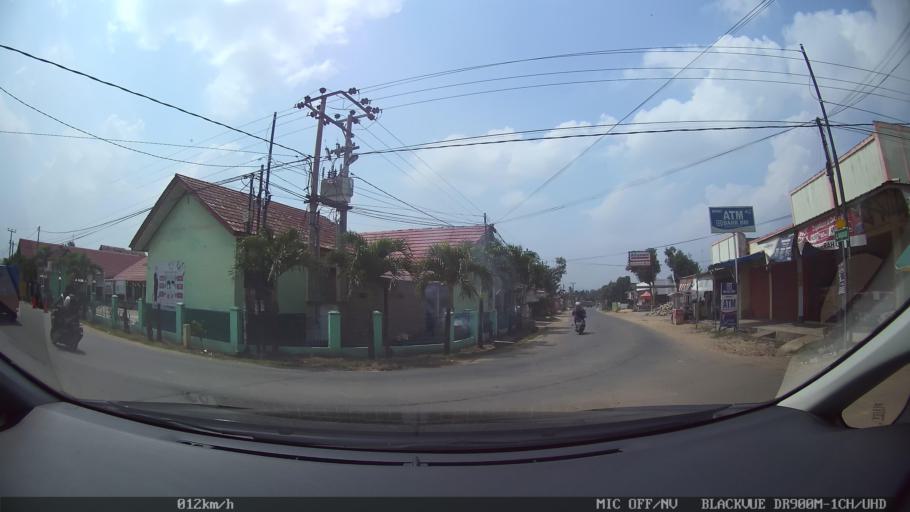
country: ID
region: Lampung
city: Pringsewu
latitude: -5.3874
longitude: 104.9607
